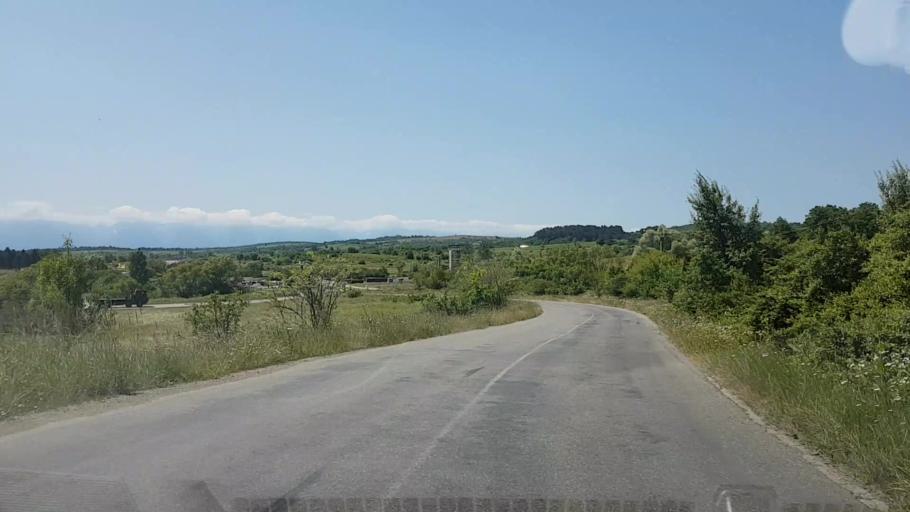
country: RO
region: Brasov
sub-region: Comuna Cincu
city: Cincu
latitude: 45.9316
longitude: 24.7957
